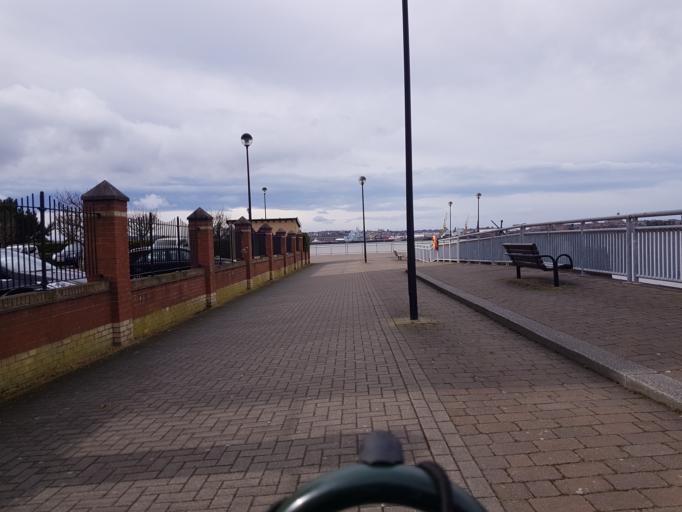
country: GB
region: England
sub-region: Liverpool
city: Liverpool
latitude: 53.3900
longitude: -2.9871
